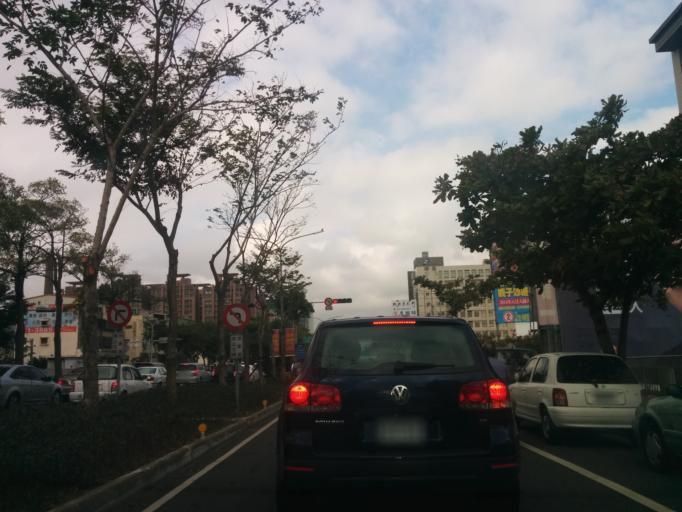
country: TW
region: Taiwan
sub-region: Hsinchu
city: Hsinchu
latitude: 24.8015
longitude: 121.0012
